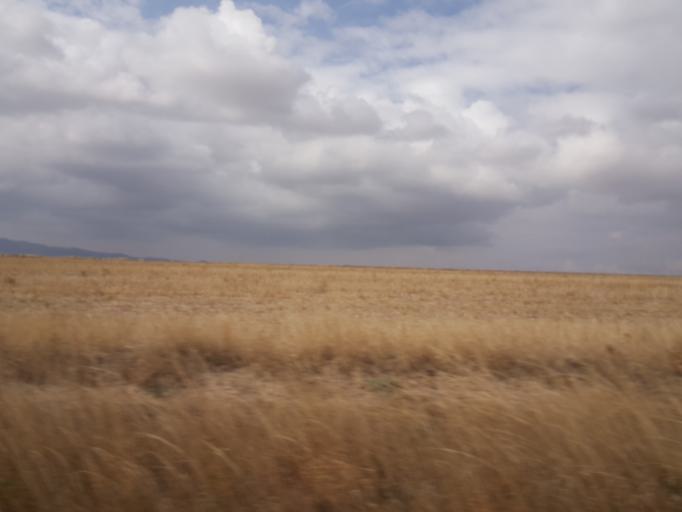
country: TR
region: Kirikkale
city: Keskin
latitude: 39.6157
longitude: 33.6129
